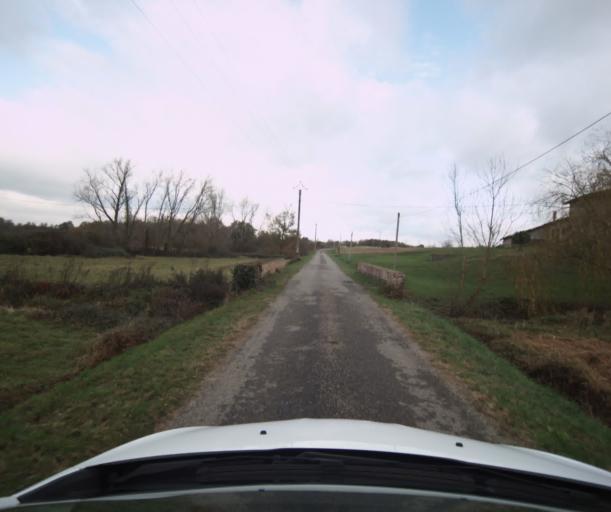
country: FR
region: Midi-Pyrenees
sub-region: Departement du Tarn-et-Garonne
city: Saint-Porquier
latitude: 44.0663
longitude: 1.1723
